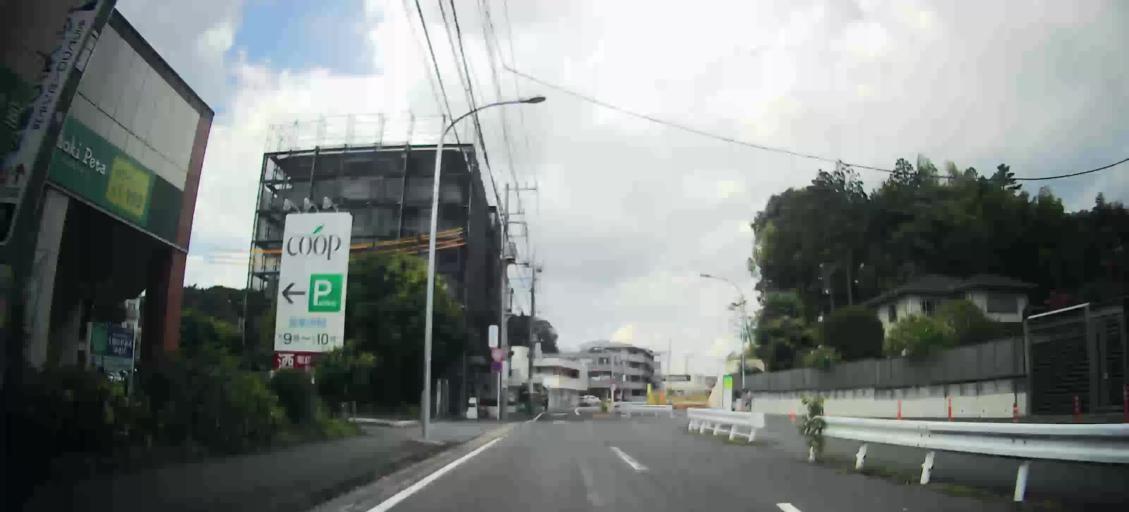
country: JP
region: Kanagawa
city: Minami-rinkan
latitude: 35.4841
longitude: 139.5453
